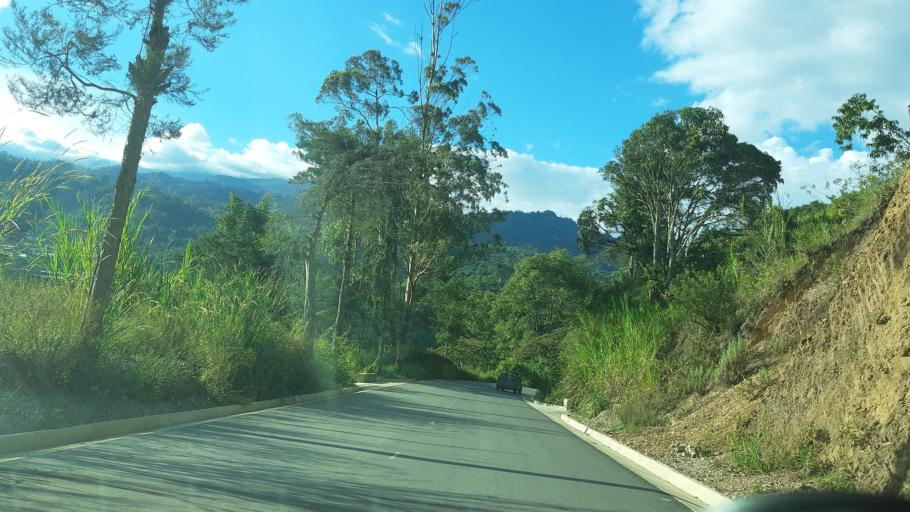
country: CO
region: Boyaca
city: Garagoa
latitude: 5.0810
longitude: -73.3810
